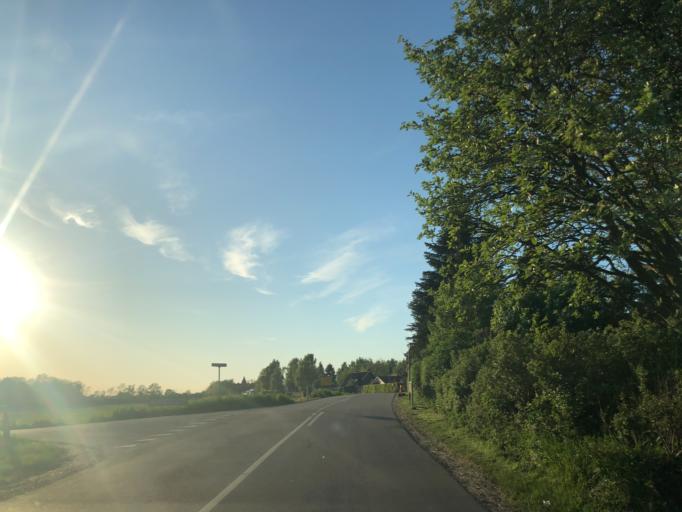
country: DK
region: Zealand
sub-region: Koge Kommune
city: Bjaeverskov
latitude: 55.4311
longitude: 12.0619
